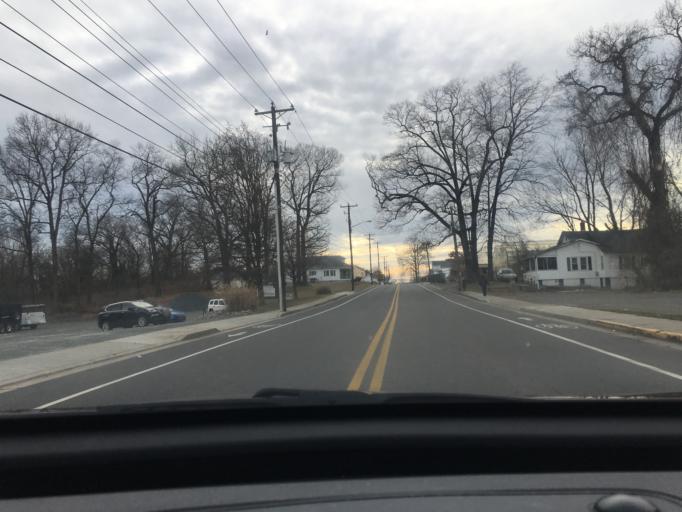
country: US
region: Maryland
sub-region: Wicomico County
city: Salisbury
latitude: 38.3709
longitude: -75.6095
